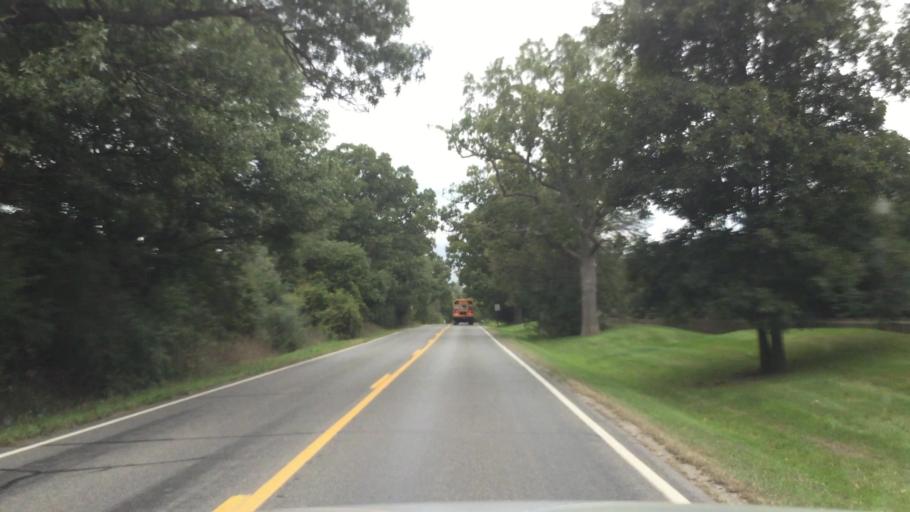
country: US
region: Michigan
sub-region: Livingston County
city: Brighton
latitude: 42.4871
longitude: -83.7677
